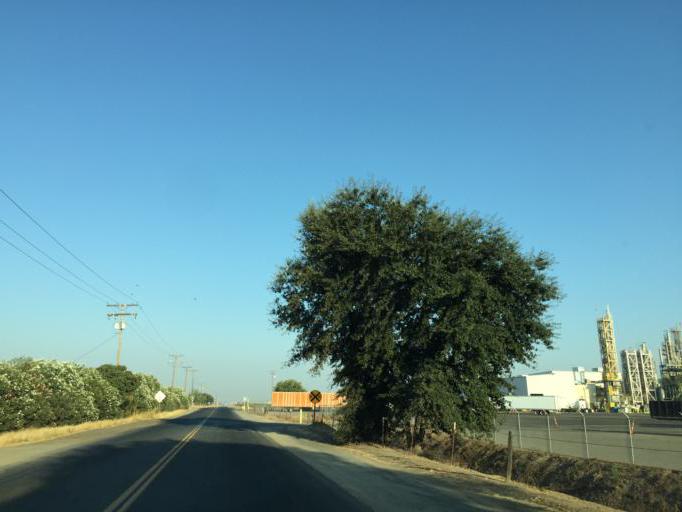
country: US
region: California
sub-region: Tulare County
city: Cutler
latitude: 36.4578
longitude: -119.2963
